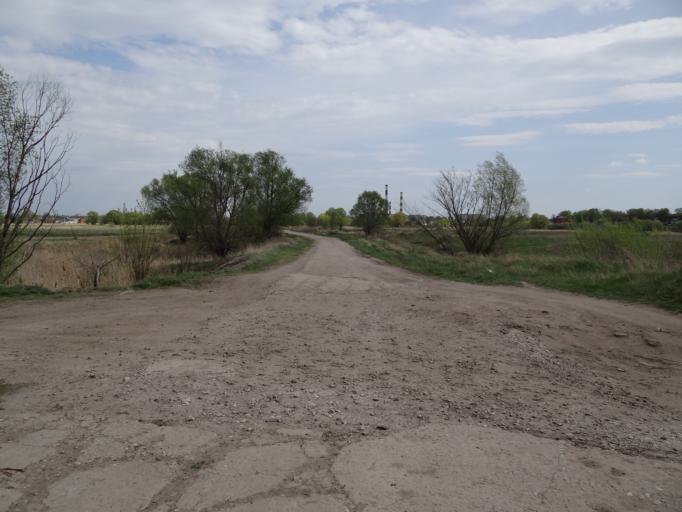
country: RU
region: Kursk
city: Voroshnevo
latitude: 51.6791
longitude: 36.0867
